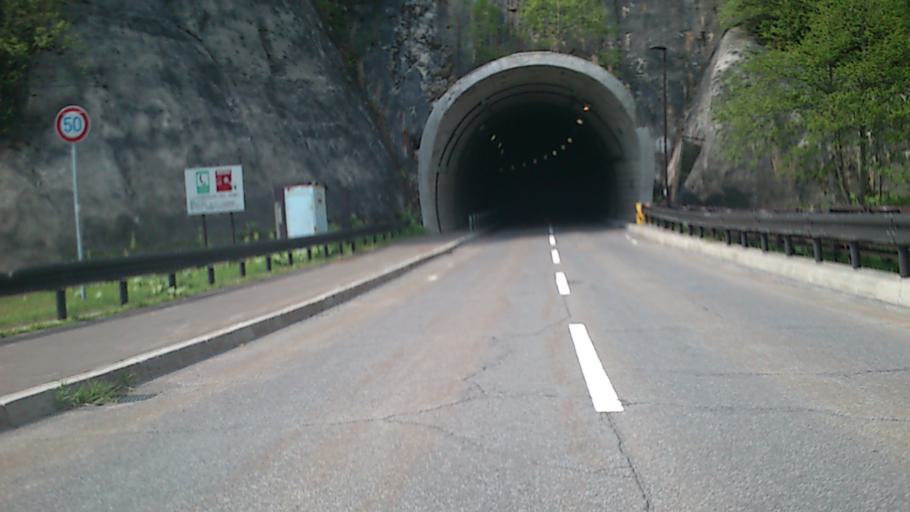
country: JP
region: Hokkaido
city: Kamikawa
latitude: 43.6751
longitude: 143.0357
